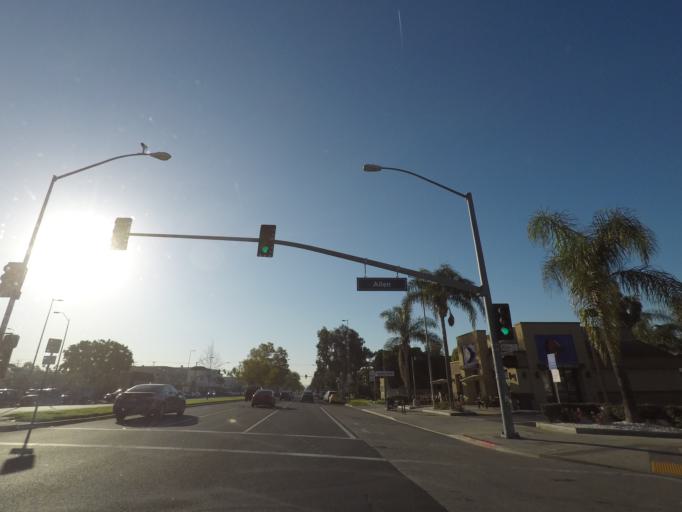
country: US
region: California
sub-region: Los Angeles County
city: Burbank
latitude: 34.1739
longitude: -118.2938
